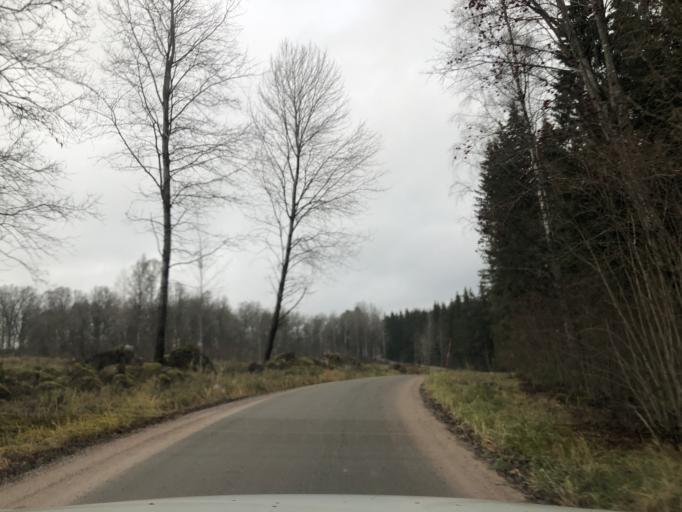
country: SE
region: Vaestra Goetaland
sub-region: Ulricehamns Kommun
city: Ulricehamn
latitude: 57.8447
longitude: 13.6369
